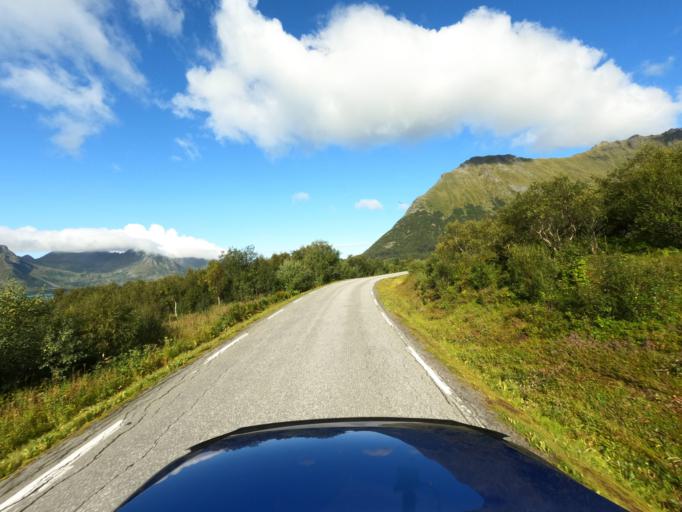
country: NO
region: Nordland
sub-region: Vagan
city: Kabelvag
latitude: 68.2785
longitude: 14.3532
